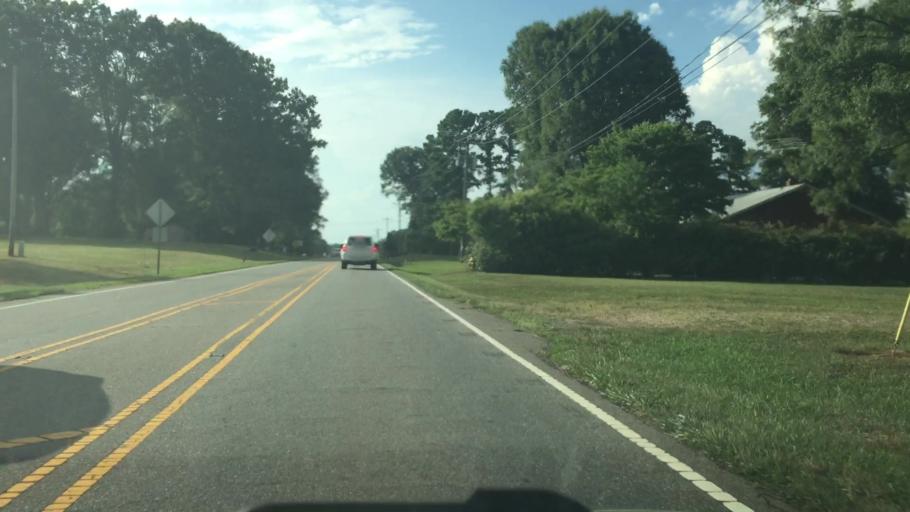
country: US
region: North Carolina
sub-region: Iredell County
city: Mooresville
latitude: 35.5461
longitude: -80.7712
